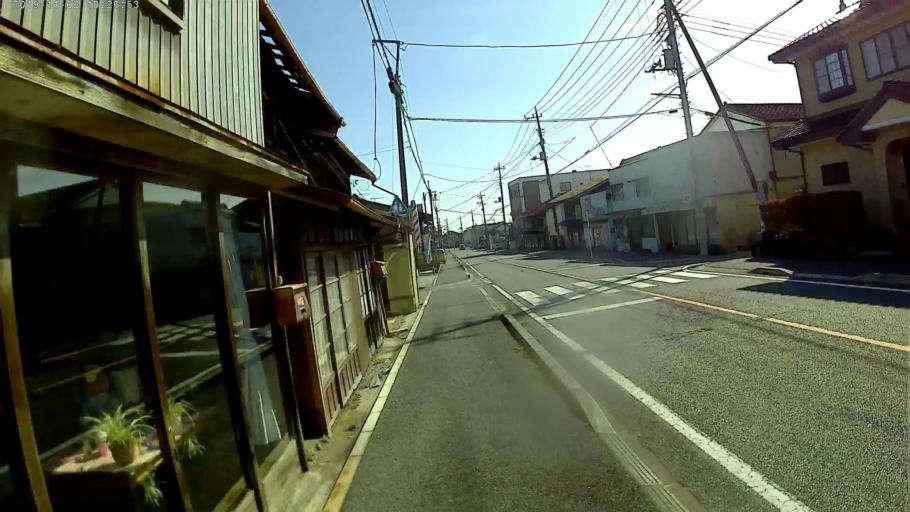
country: JP
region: Gunma
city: Annaka
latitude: 36.3125
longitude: 138.8028
